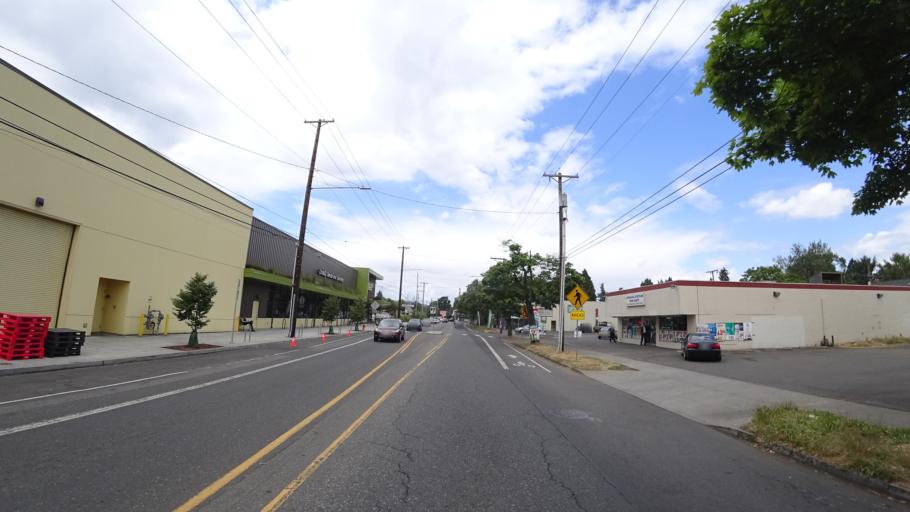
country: US
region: Oregon
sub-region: Washington County
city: West Haven
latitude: 45.5849
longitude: -122.7305
